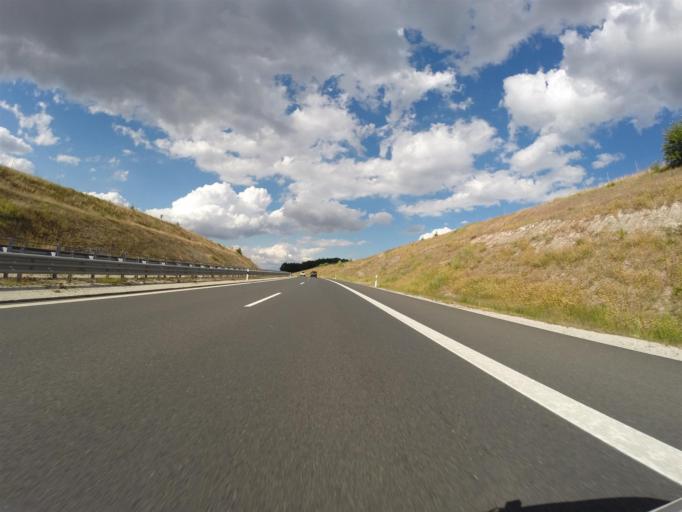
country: DE
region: Bavaria
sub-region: Upper Franconia
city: Lichtenfels
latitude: 50.1797
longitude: 11.0226
